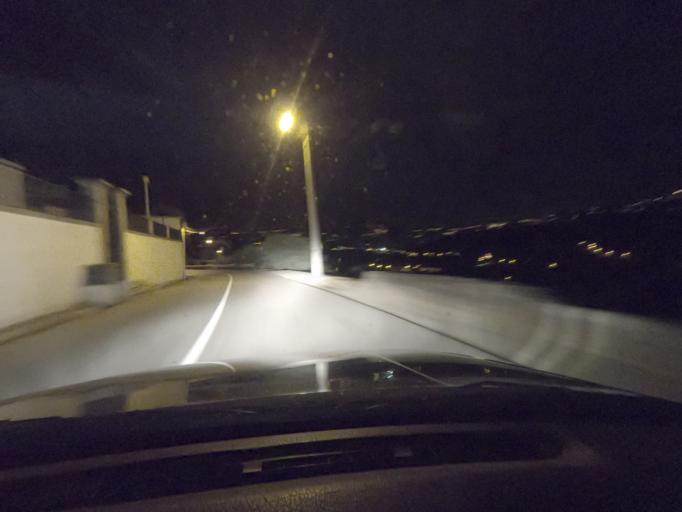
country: PT
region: Vila Real
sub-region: Santa Marta de Penaguiao
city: Santa Marta de Penaguiao
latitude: 41.2069
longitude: -7.8041
